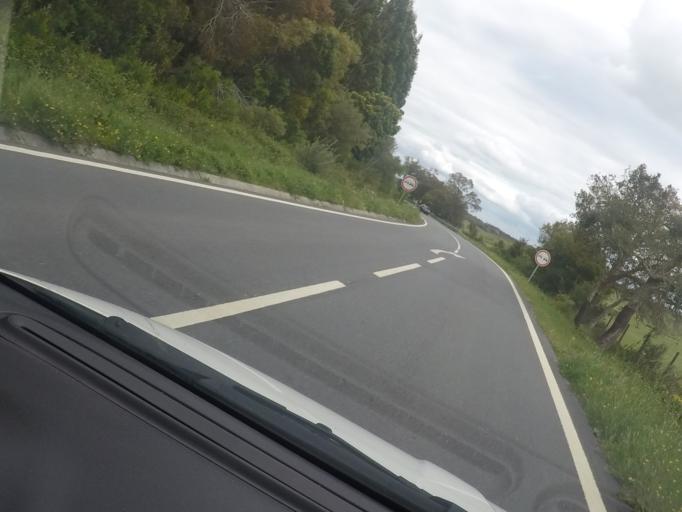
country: PT
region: Setubal
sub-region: Santiago do Cacem
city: Cercal
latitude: 37.7870
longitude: -8.7050
